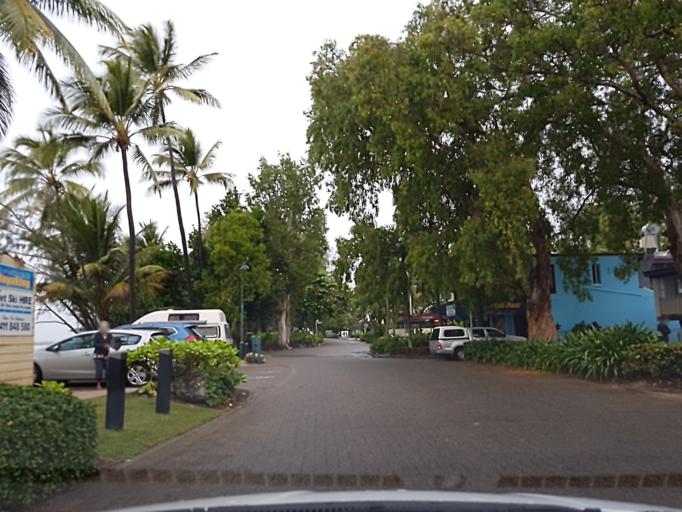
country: AU
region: Queensland
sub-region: Cairns
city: Palm Cove
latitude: -16.7465
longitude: 145.6711
